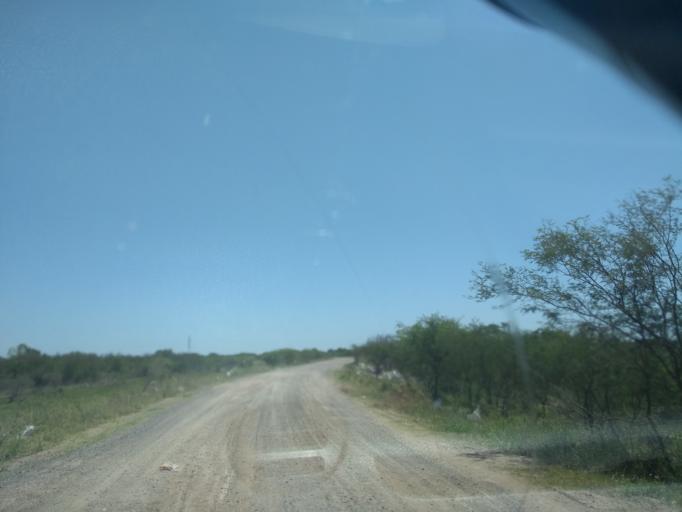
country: AR
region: Chaco
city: Resistencia
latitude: -27.4006
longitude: -58.9598
